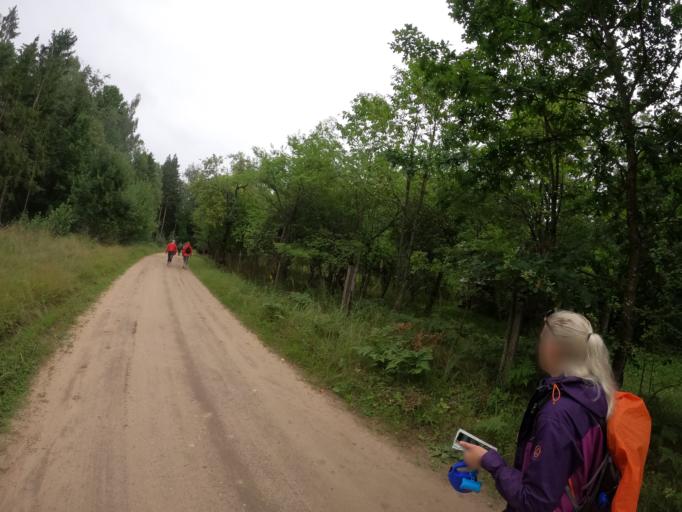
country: LV
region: Kuldigas Rajons
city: Kuldiga
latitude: 57.0162
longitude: 21.9893
